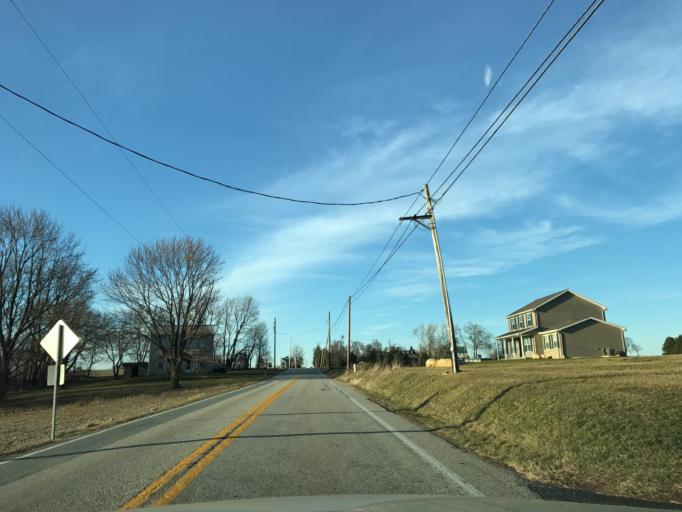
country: US
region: Pennsylvania
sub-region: Lancaster County
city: Maytown
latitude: 40.0858
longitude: -76.5910
